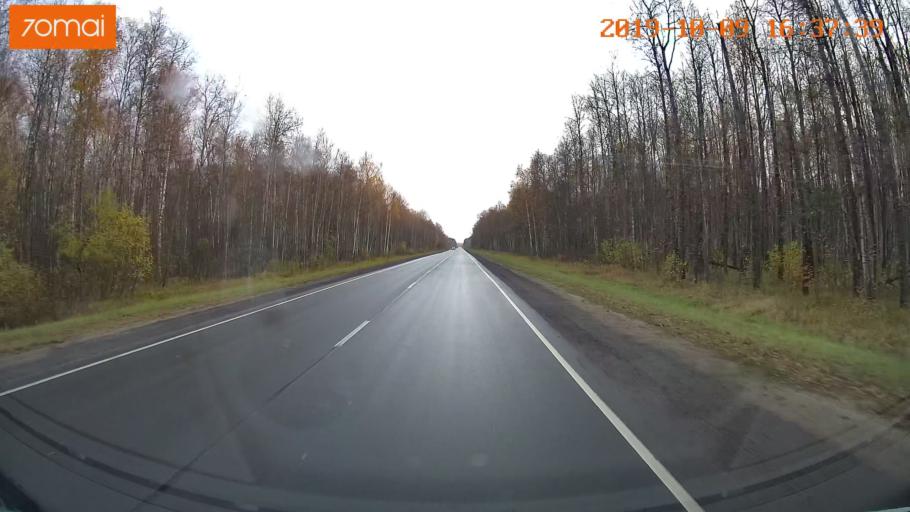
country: RU
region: Kostroma
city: Volgorechensk
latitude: 57.5238
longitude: 41.0273
